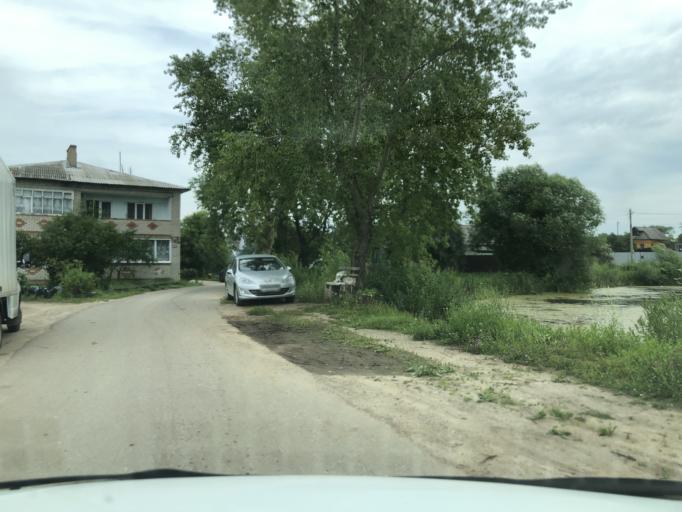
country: RU
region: Jaroslavl
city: Petrovsk
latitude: 57.0069
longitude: 39.2635
